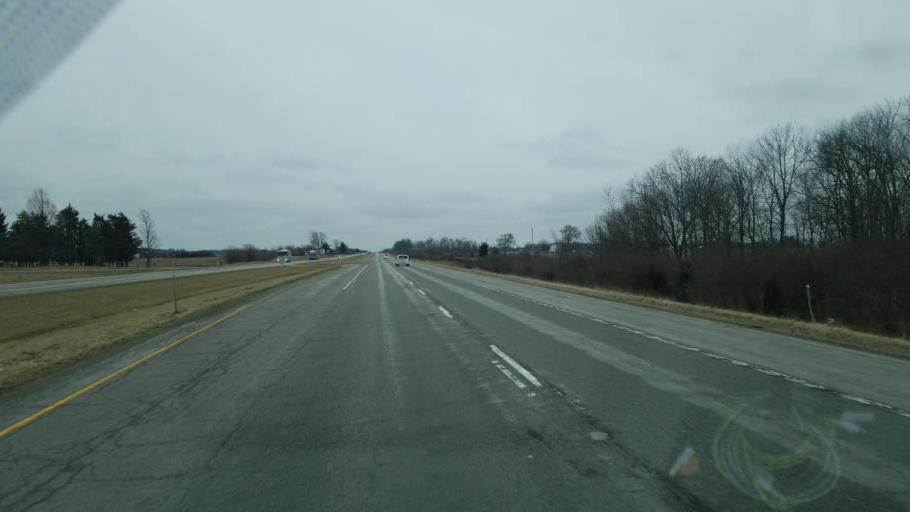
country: US
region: Indiana
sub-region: Fulton County
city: Rochester
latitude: 41.0047
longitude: -86.1679
